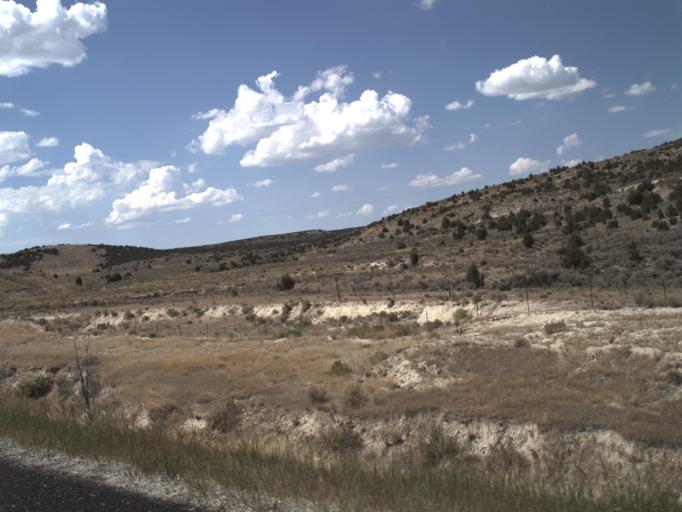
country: US
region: Idaho
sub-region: Minidoka County
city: Rupert
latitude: 41.9725
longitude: -113.1512
